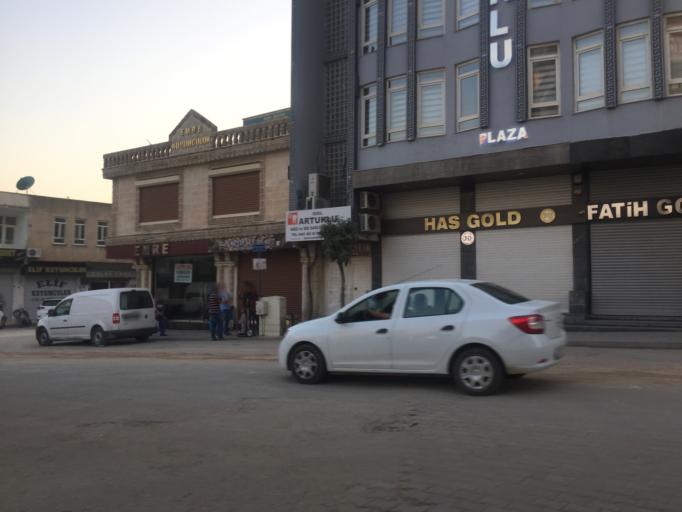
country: TR
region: Mardin
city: Midyat
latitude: 37.4249
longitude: 41.3391
